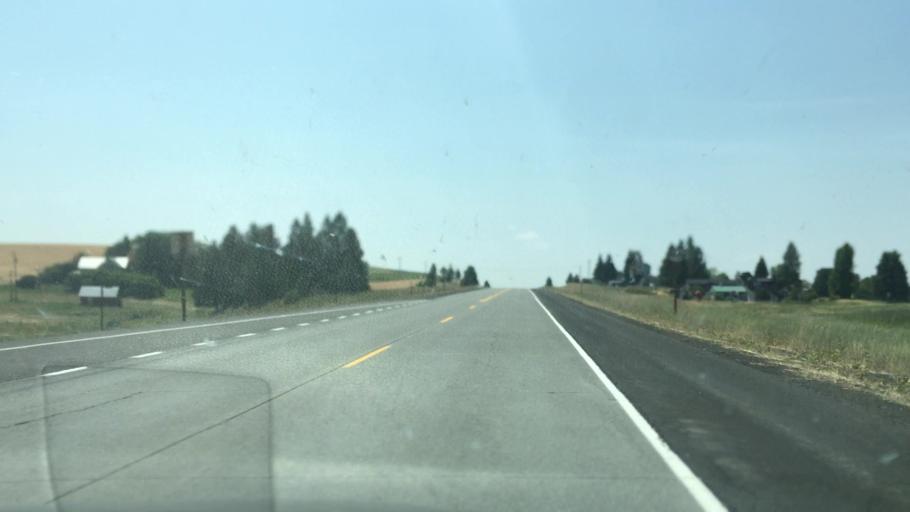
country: US
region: Idaho
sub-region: Lewis County
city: Nezperce
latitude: 46.0594
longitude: -116.3433
